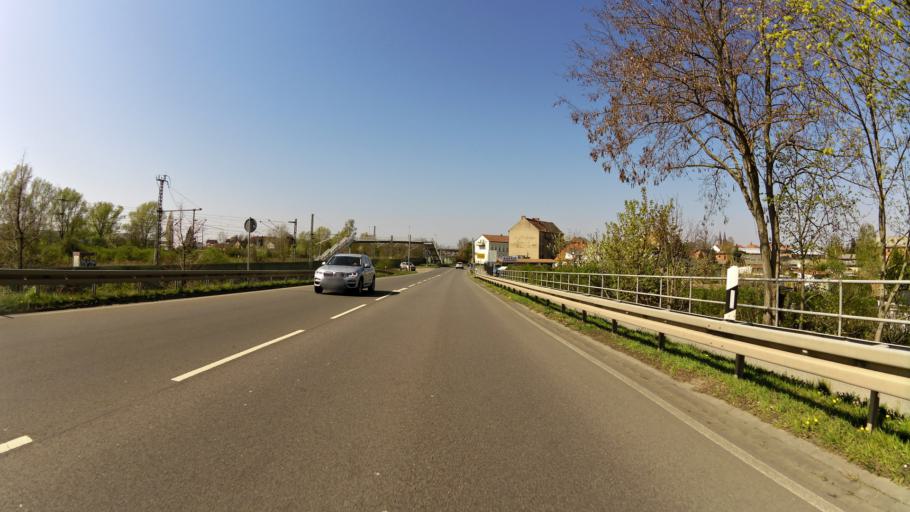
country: DE
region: Saxony-Anhalt
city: Stendal
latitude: 52.5961
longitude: 11.8730
